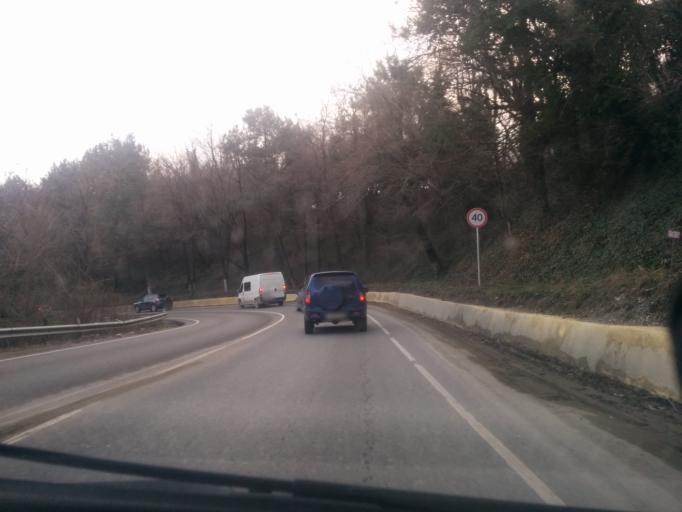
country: RU
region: Krasnodarskiy
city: Agoy
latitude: 44.1233
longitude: 39.0491
